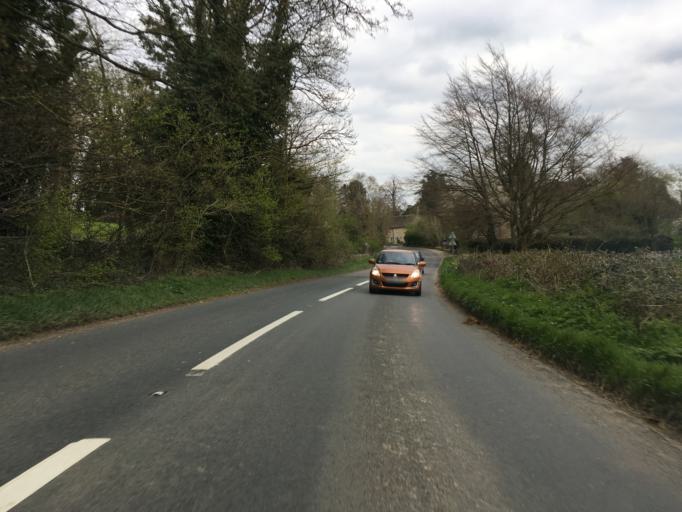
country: GB
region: England
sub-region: Gloucestershire
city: Cirencester
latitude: 51.7424
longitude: -1.8934
